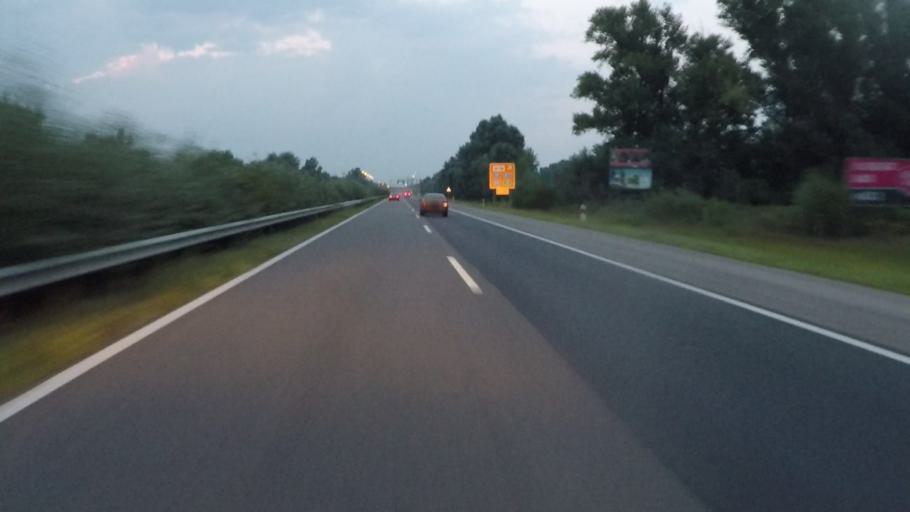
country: HU
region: Pest
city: Gyal
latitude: 47.3877
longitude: 19.1744
